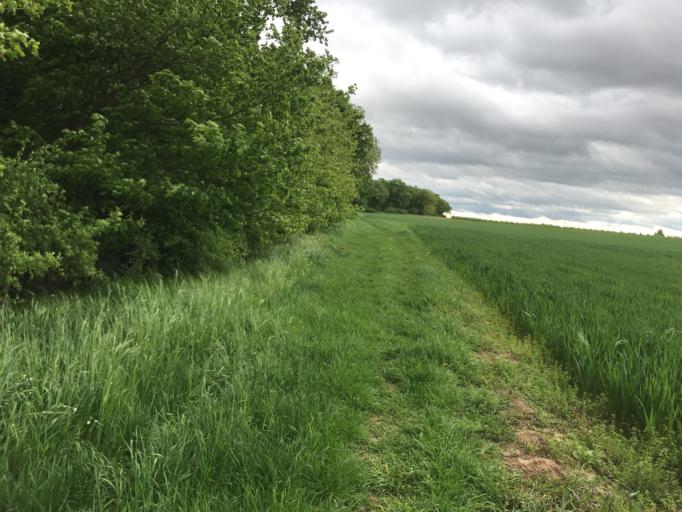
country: DE
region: Rheinland-Pfalz
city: Ober-Olm
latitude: 49.9514
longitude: 8.1703
